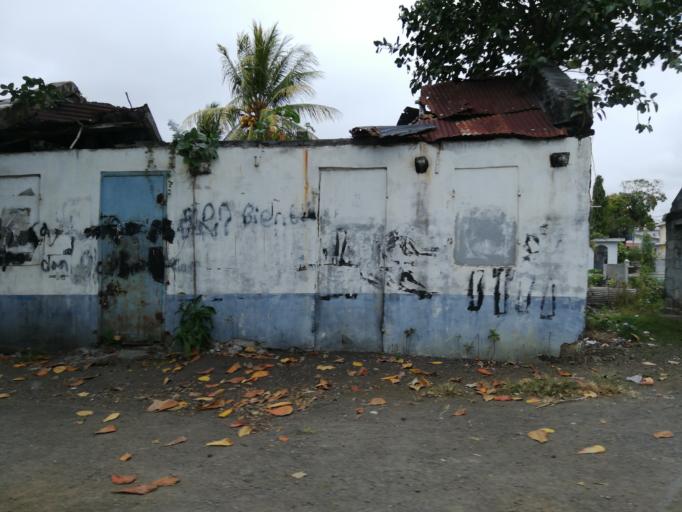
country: MU
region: Flacq
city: Poste de Flacq
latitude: -20.1705
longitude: 57.7315
